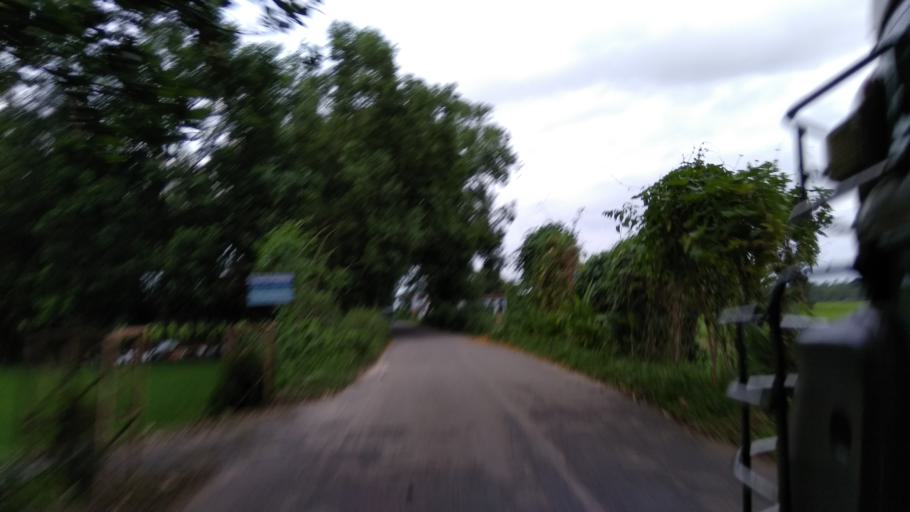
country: IN
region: Tripura
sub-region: Dhalai
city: Kamalpur
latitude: 24.2210
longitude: 91.8547
